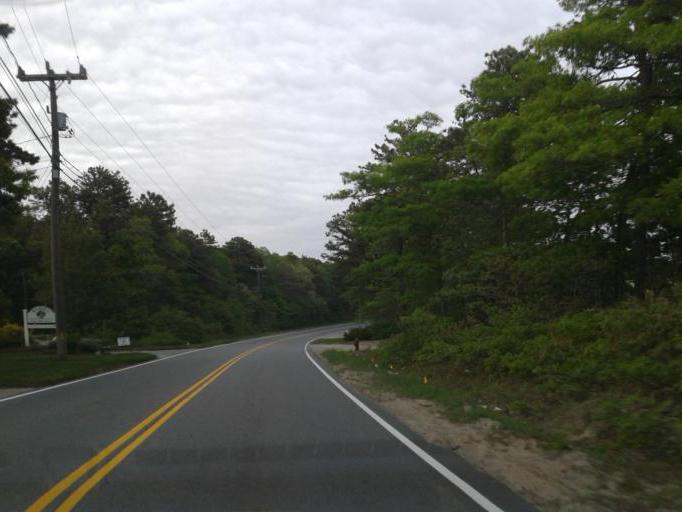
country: US
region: Massachusetts
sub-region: Barnstable County
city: West Falmouth
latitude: 41.6151
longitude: -70.6047
